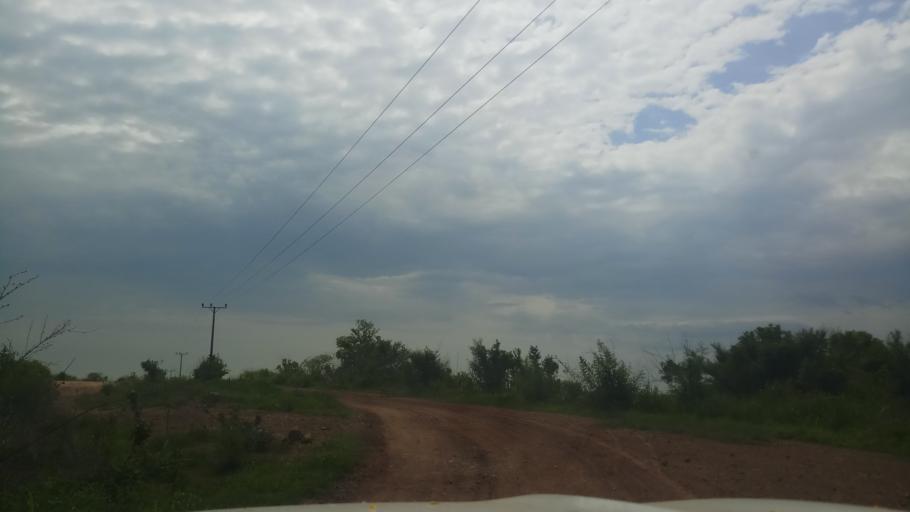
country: ET
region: Gambela
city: Gambela
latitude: 8.2155
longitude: 34.5519
